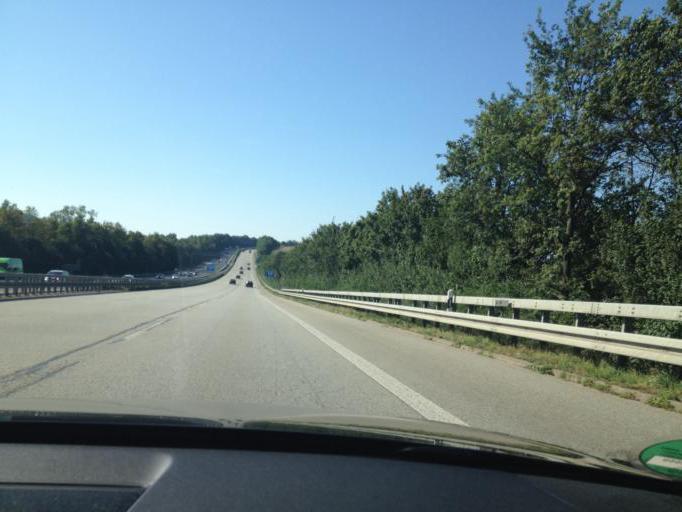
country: DE
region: Baden-Wuerttemberg
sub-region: Regierungsbezirk Stuttgart
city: Ilsfeld
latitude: 49.0567
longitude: 9.2685
